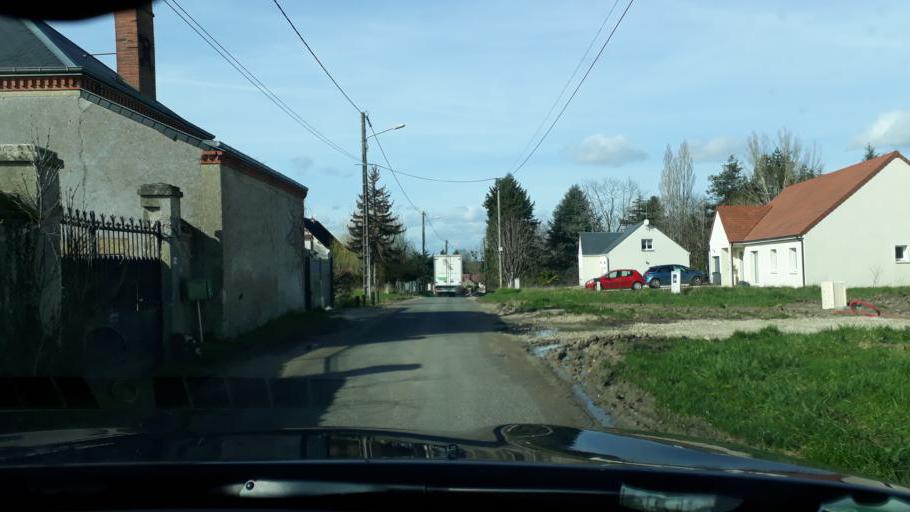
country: FR
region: Centre
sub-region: Departement du Loiret
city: Donnery
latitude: 47.9118
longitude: 2.1105
